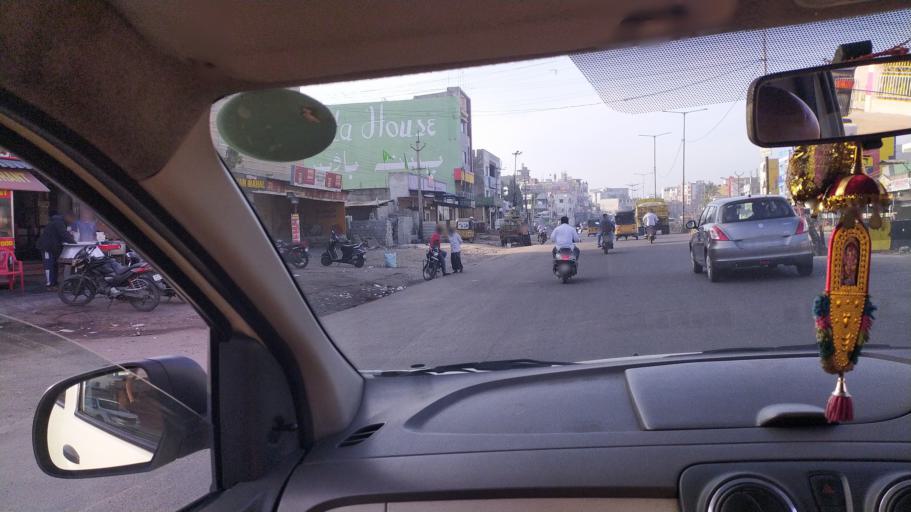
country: IN
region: Telangana
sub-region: Rangareddi
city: Balapur
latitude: 17.3186
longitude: 78.4669
